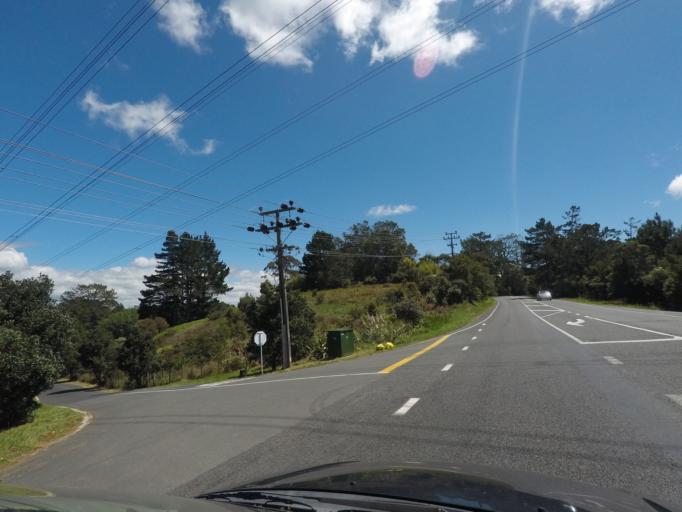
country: NZ
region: Auckland
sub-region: Auckland
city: Rothesay Bay
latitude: -36.7358
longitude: 174.6757
